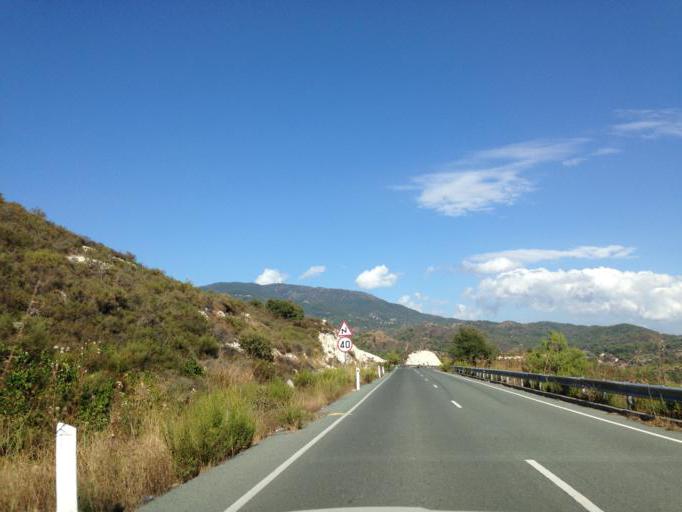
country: CY
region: Limassol
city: Pachna
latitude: 34.8626
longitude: 32.8113
